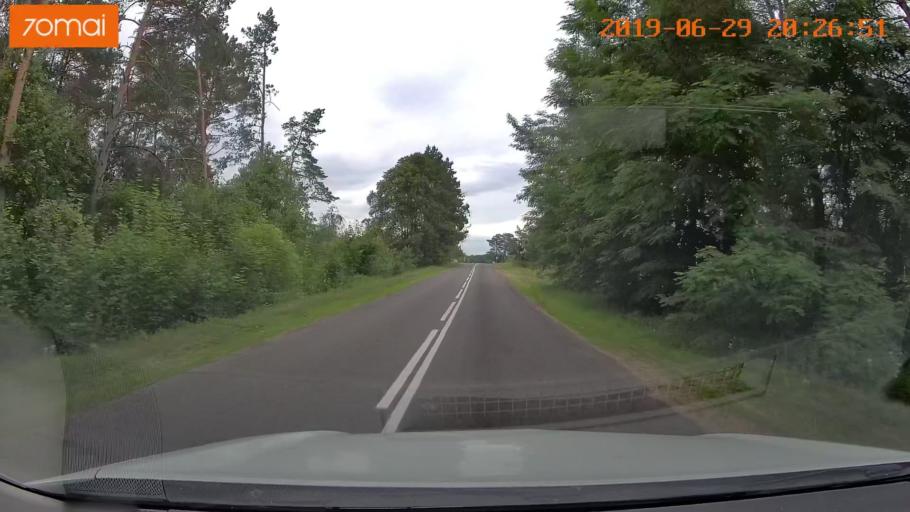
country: BY
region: Brest
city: Hantsavichy
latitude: 52.4699
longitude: 26.2995
